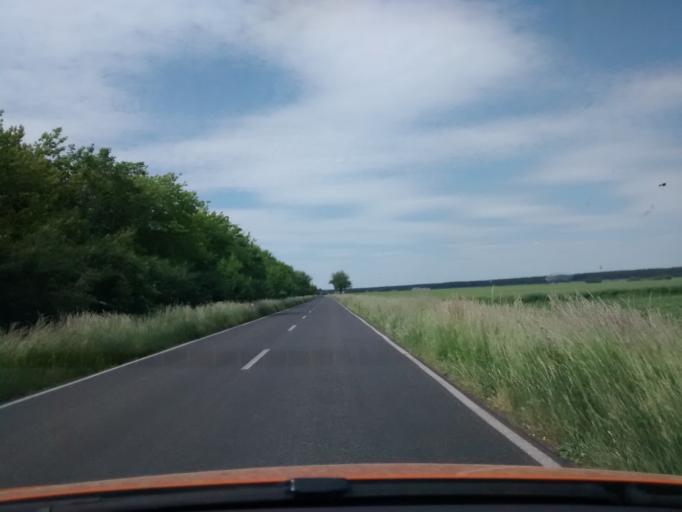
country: DE
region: Brandenburg
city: Ihlow
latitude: 51.9355
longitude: 13.3364
